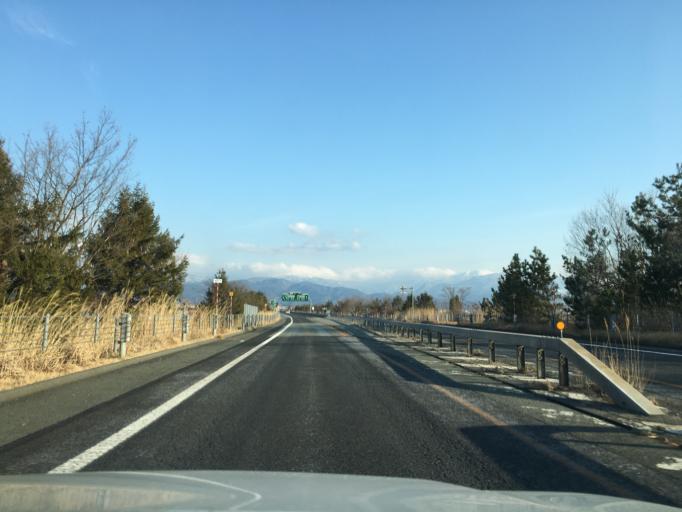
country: JP
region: Yamagata
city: Sagae
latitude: 38.3170
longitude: 140.3058
